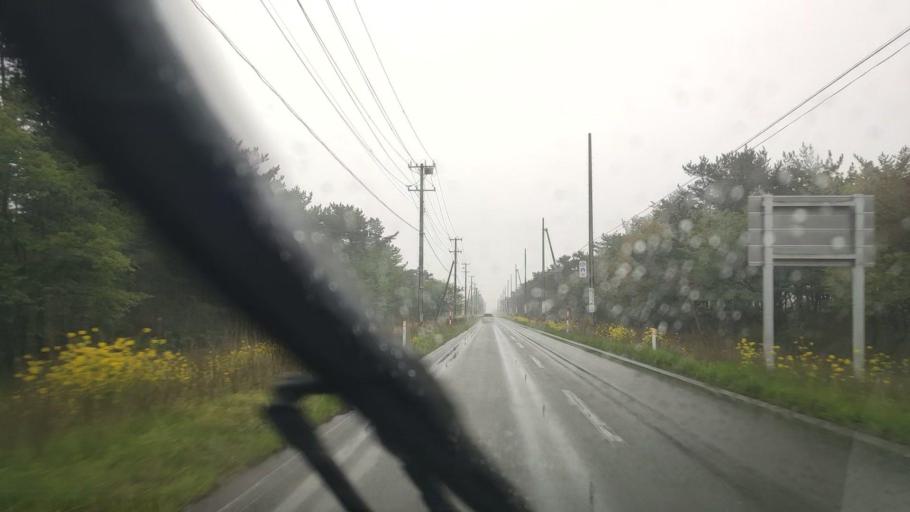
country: JP
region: Akita
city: Tenno
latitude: 40.0073
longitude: 139.9501
